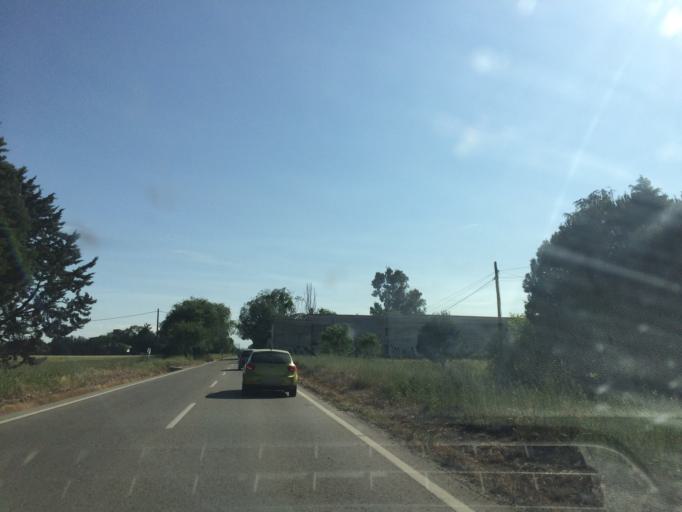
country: ES
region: Madrid
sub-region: Provincia de Madrid
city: Fuente el Saz
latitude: 40.6479
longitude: -3.5014
